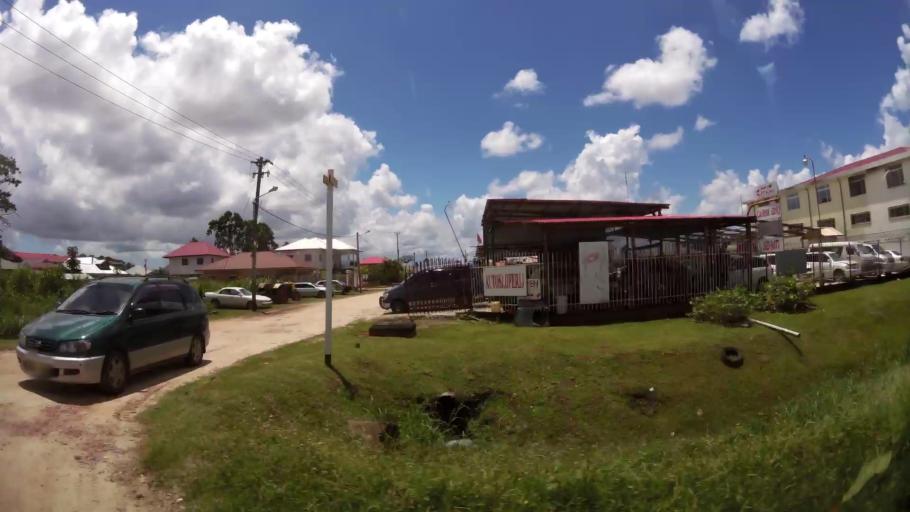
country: SR
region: Paramaribo
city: Paramaribo
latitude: 5.8545
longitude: -55.1665
